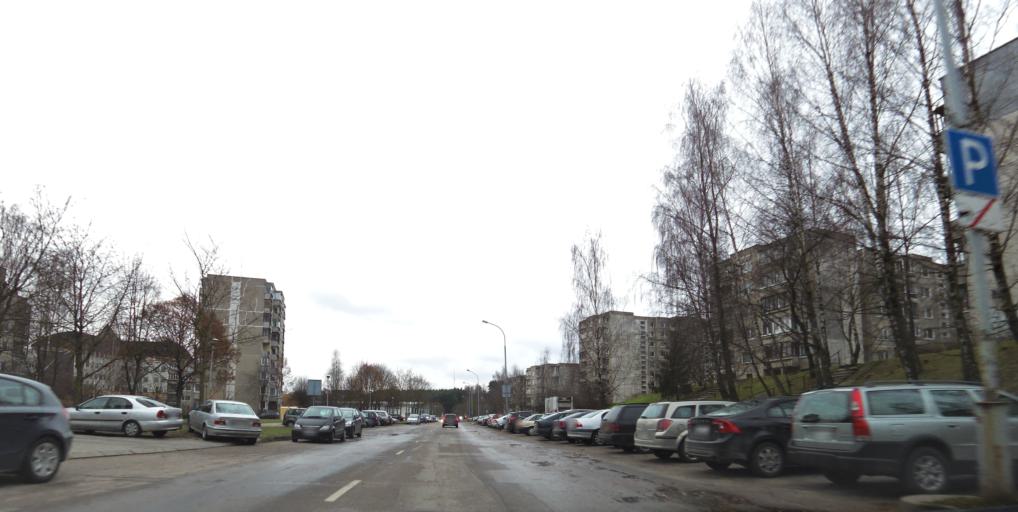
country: LT
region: Vilnius County
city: Justiniskes
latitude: 54.7188
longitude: 25.2293
